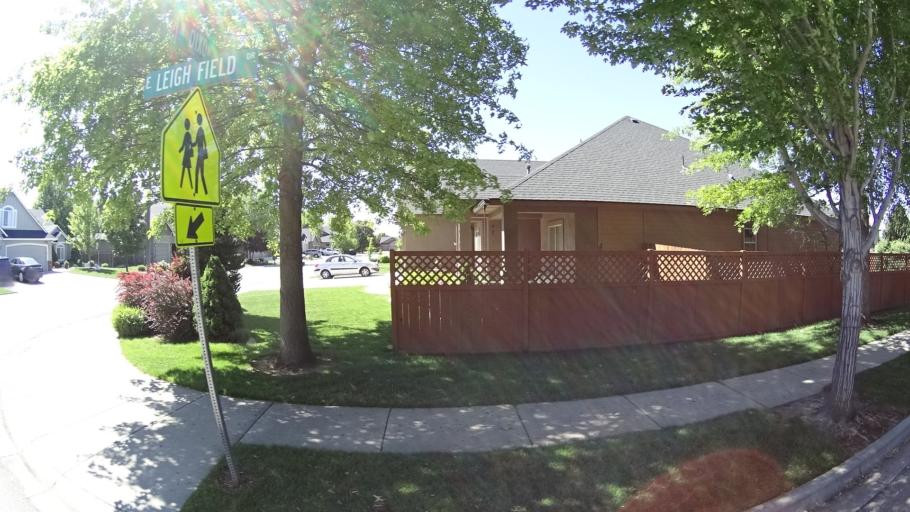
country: US
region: Idaho
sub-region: Ada County
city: Meridian
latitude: 43.6393
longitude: -116.3668
